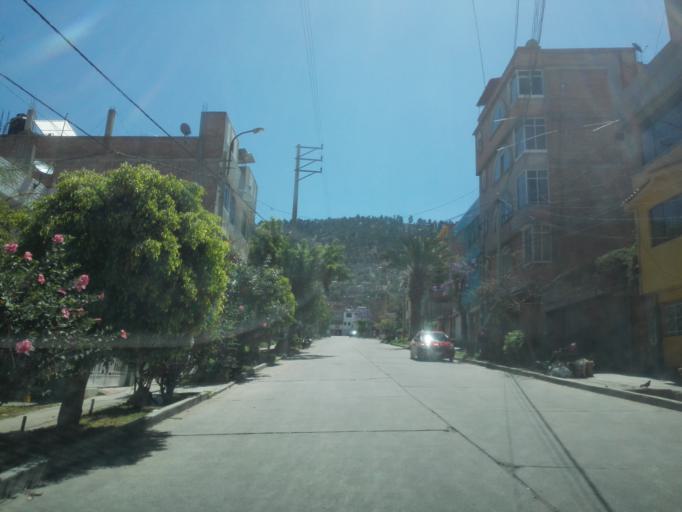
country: PE
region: Ayacucho
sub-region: Provincia de Huamanga
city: Ayacucho
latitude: -13.1528
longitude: -74.2285
